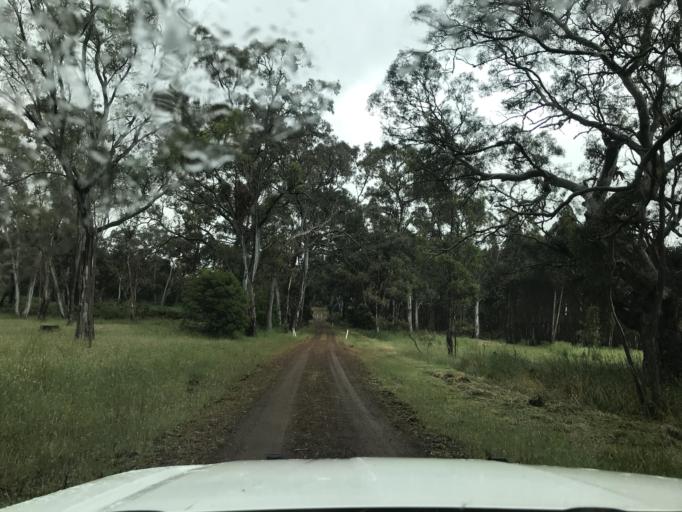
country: AU
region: South Australia
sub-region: Wattle Range
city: Penola
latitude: -37.2536
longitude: 141.3386
